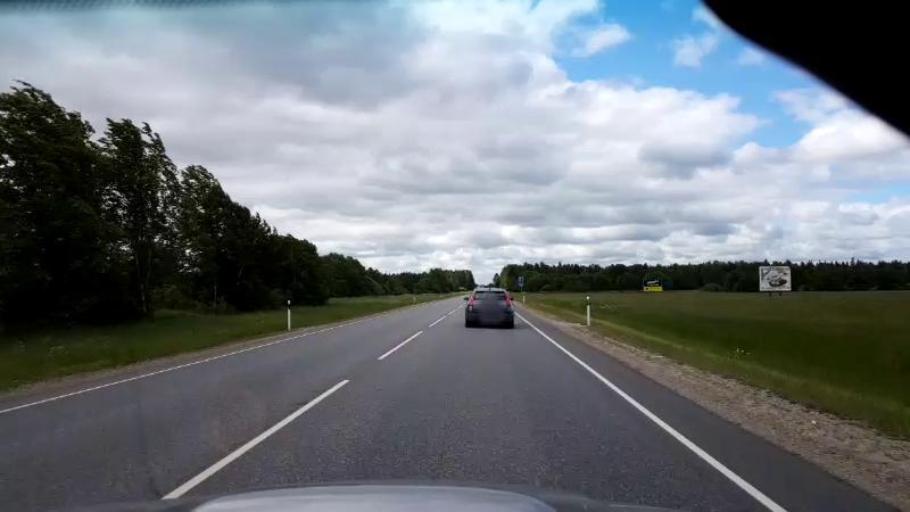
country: EE
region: Raplamaa
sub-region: Maerjamaa vald
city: Marjamaa
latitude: 58.9413
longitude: 24.4663
